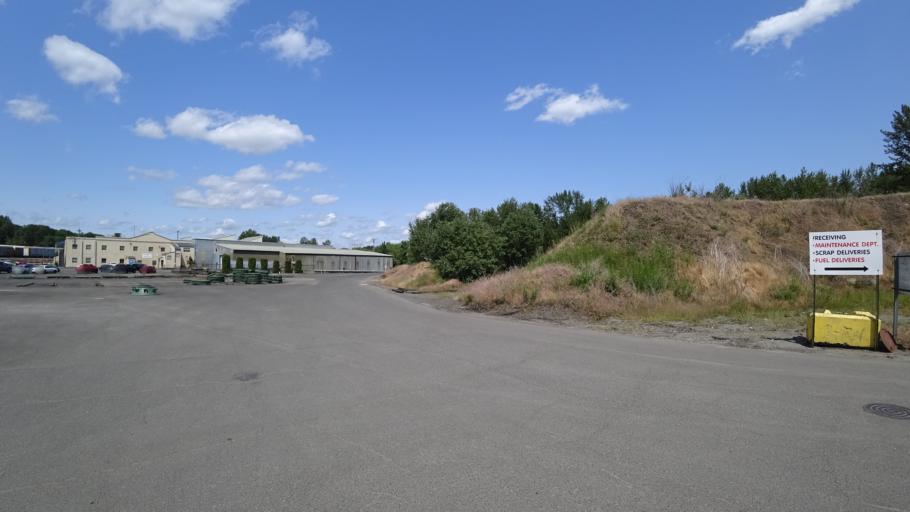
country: US
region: Washington
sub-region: Clark County
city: Vancouver
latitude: 45.6009
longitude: -122.7304
